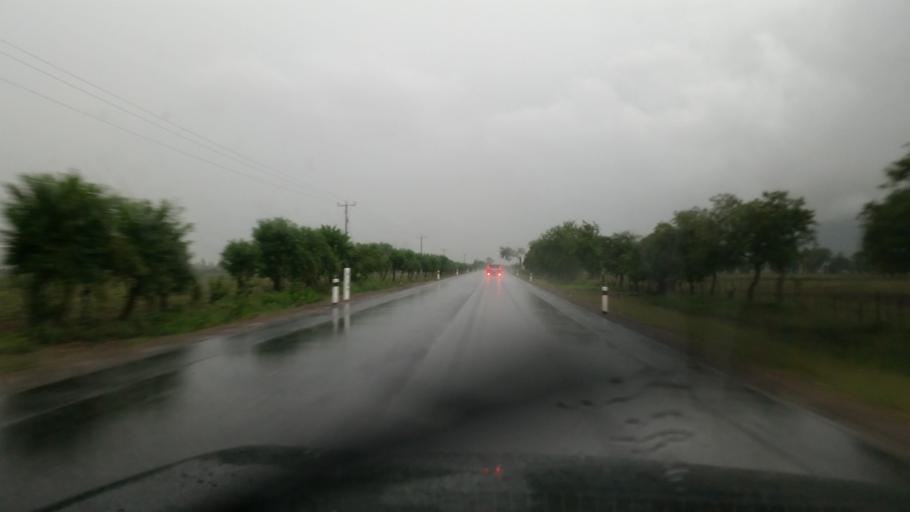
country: NI
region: Chinandega
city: Chichigalpa
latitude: 12.7759
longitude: -86.9227
